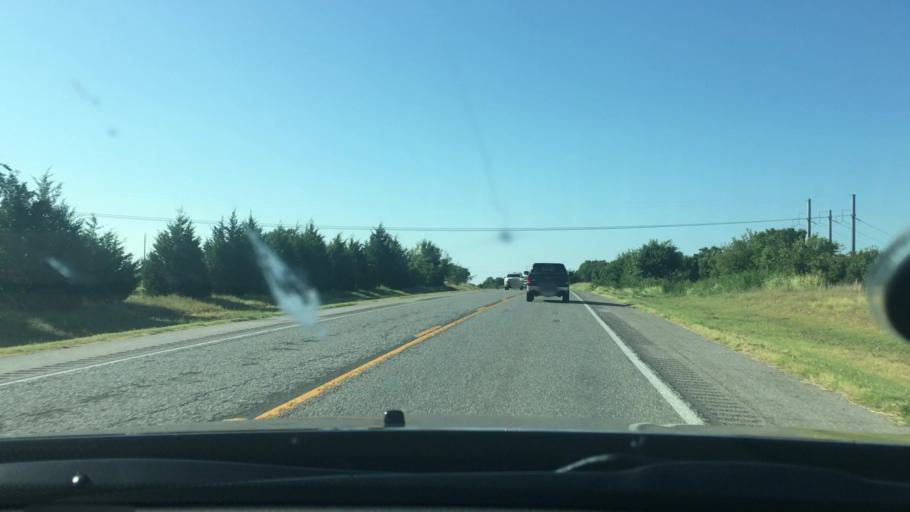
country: US
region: Oklahoma
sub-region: Johnston County
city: Tishomingo
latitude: 34.2660
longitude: -96.7724
